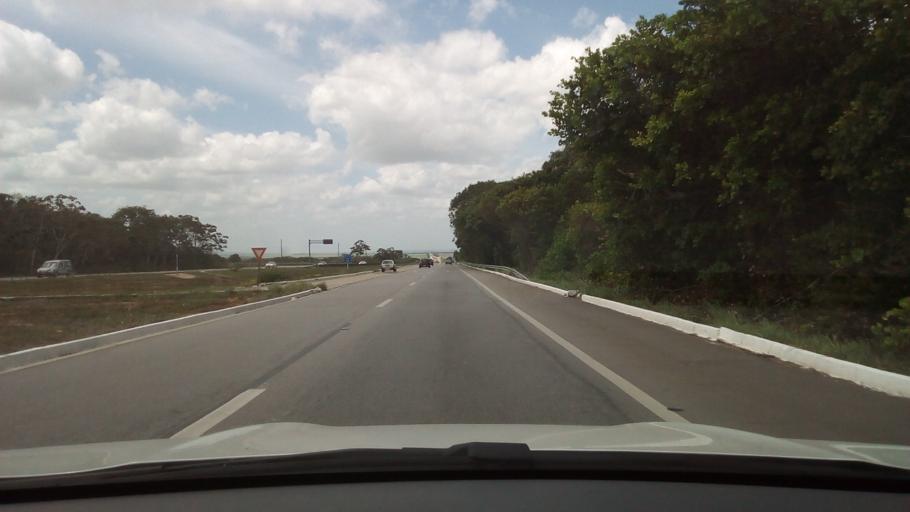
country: BR
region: Paraiba
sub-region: Mamanguape
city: Mamanguape
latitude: -6.9625
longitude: -35.0860
